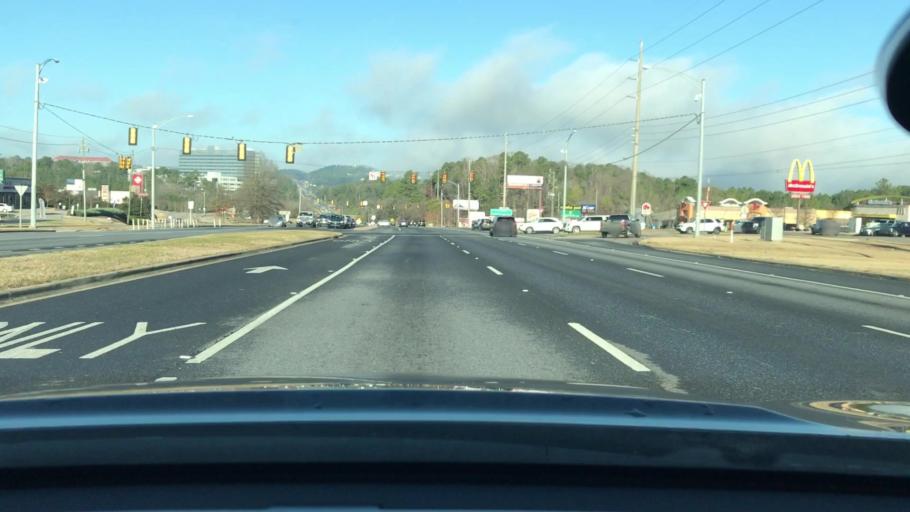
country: US
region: Alabama
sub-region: Shelby County
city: Lake Purdy
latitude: 33.4278
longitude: -86.7068
